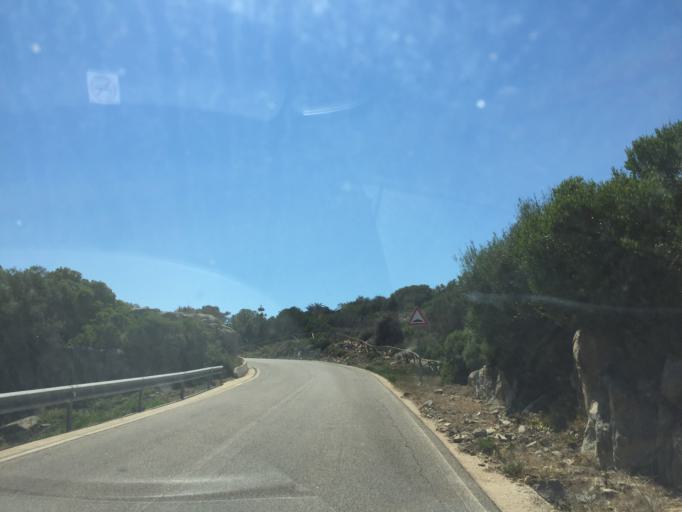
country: IT
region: Sardinia
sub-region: Provincia di Olbia-Tempio
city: Santa Teresa Gallura
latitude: 41.2371
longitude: 9.1764
